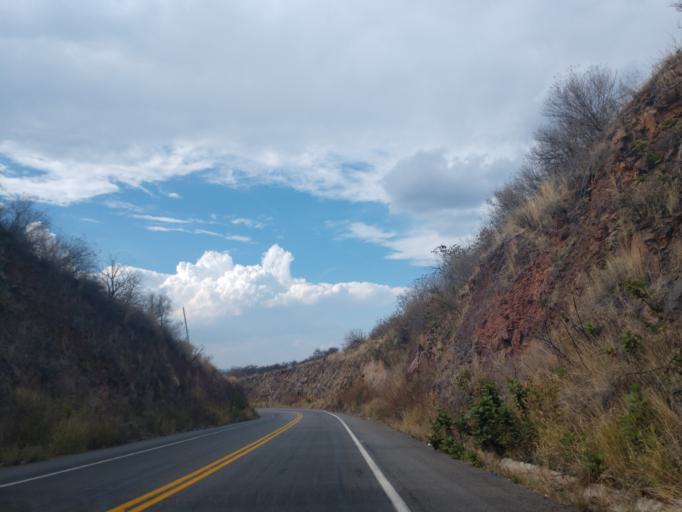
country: MX
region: Jalisco
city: La Manzanilla de la Paz
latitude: 20.0981
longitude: -103.1694
